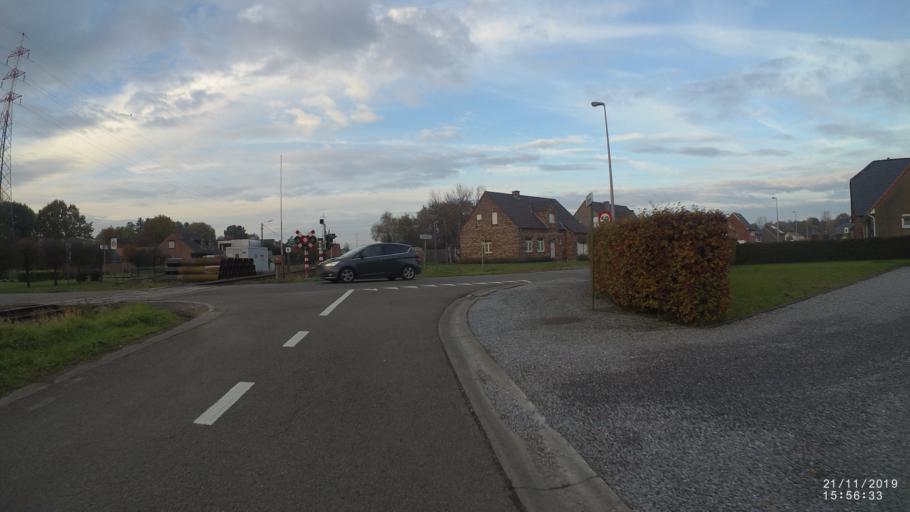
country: BE
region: Flanders
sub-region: Provincie Limburg
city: Zonhoven
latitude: 50.9993
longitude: 5.3485
